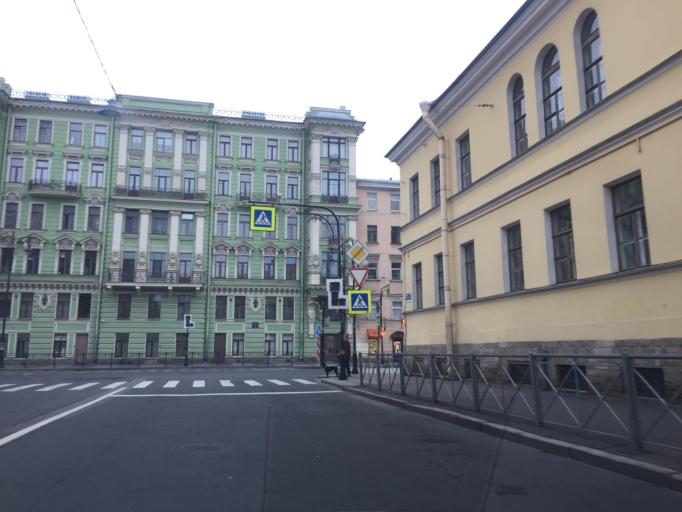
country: RU
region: St.-Petersburg
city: Centralniy
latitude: 59.9436
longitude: 30.3638
